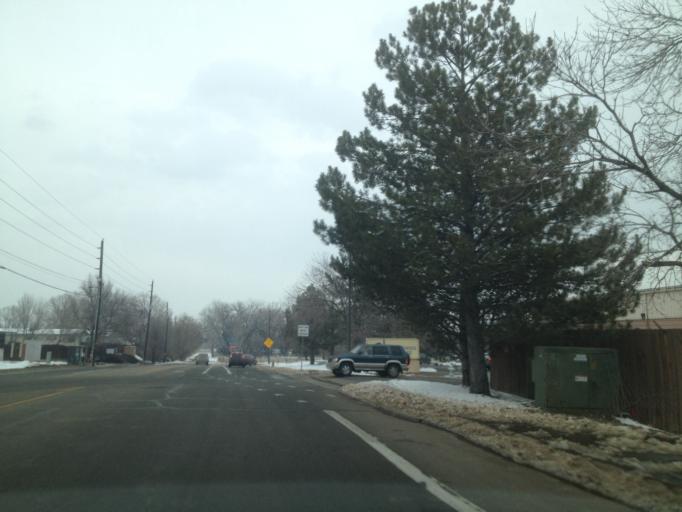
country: US
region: Colorado
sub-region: Boulder County
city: Boulder
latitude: 40.0292
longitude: -105.2269
